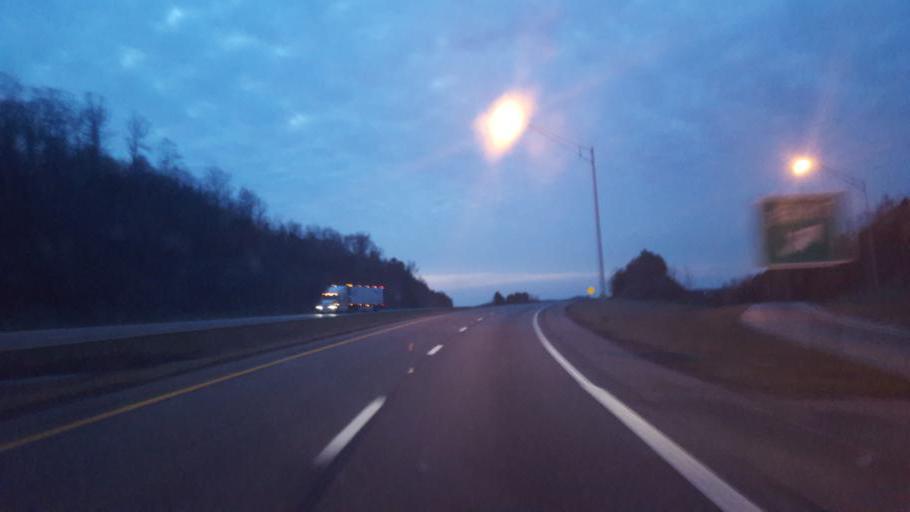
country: US
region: Ohio
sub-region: Jackson County
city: Jackson
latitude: 39.0583
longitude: -82.6179
